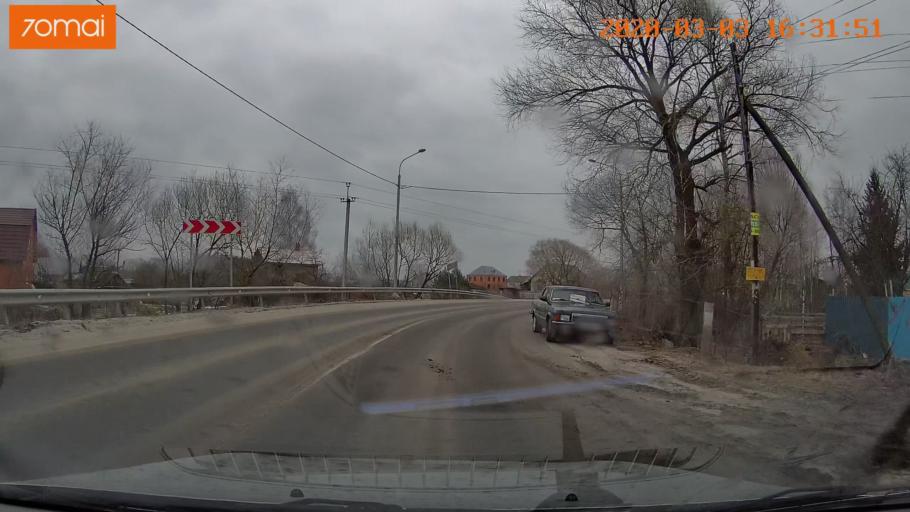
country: RU
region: Moskovskaya
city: Konobeyevo
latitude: 55.4236
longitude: 38.7287
